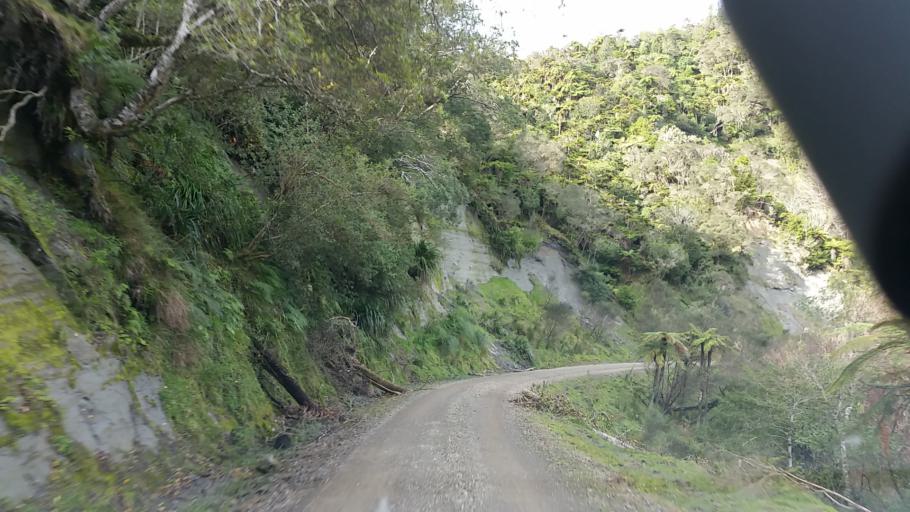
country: NZ
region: Taranaki
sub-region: New Plymouth District
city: Waitara
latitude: -39.0637
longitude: 174.5614
